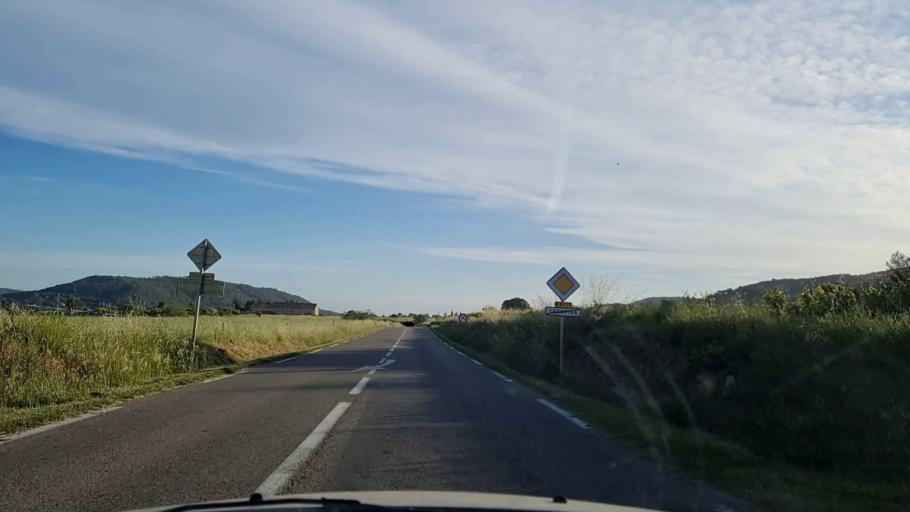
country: FR
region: Languedoc-Roussillon
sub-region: Departement du Gard
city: Saint-Mamert-du-Gard
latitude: 43.8857
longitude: 4.0981
